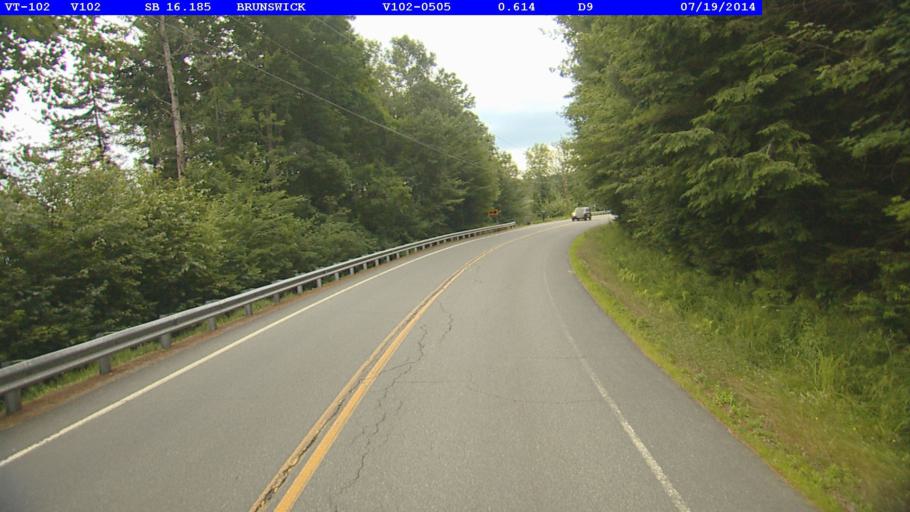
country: US
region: New Hampshire
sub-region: Coos County
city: Stratford
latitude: 44.6703
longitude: -71.5941
